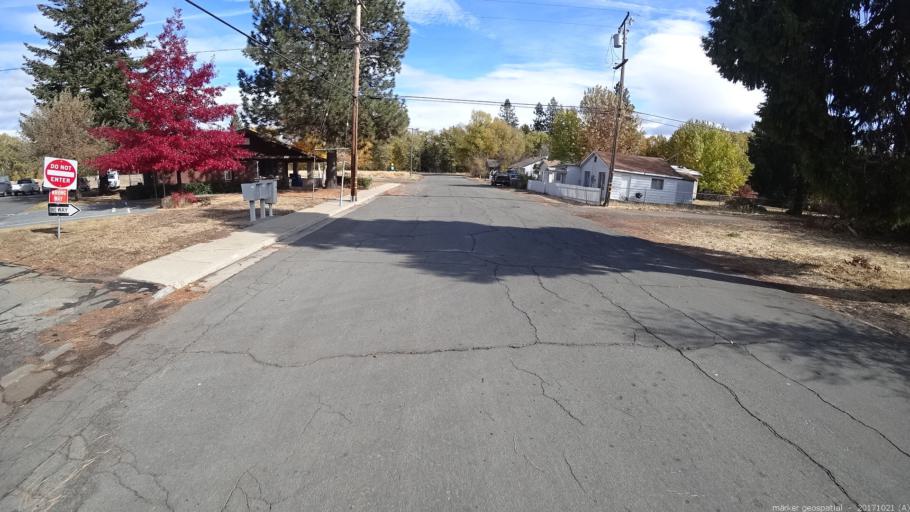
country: US
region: California
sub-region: Shasta County
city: Burney
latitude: 40.8845
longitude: -121.6702
